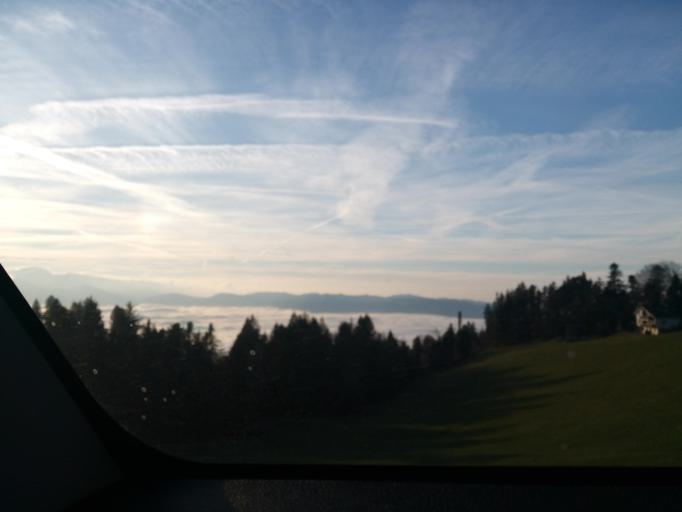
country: AT
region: Vorarlberg
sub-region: Politischer Bezirk Bregenz
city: Bildstein
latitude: 47.4305
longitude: 9.7833
